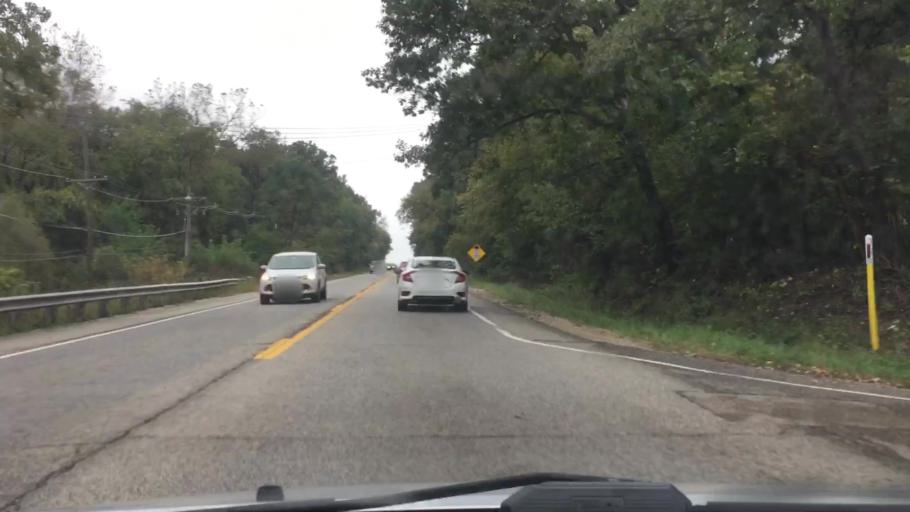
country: US
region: Illinois
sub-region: McHenry County
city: Prairie Grove
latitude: 42.2639
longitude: -88.2868
